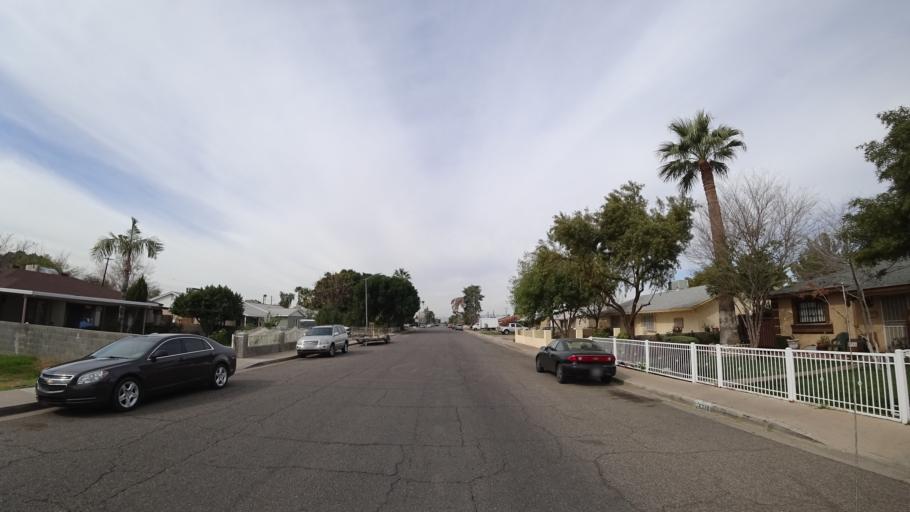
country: US
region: Arizona
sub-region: Maricopa County
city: Glendale
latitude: 33.5348
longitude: -112.1957
